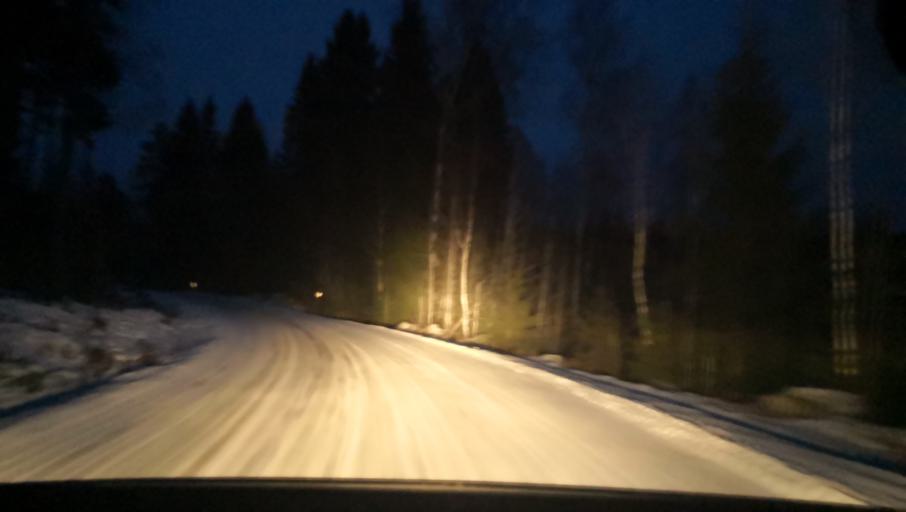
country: SE
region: Uppsala
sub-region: Heby Kommun
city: Tarnsjo
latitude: 60.2572
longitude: 16.7739
